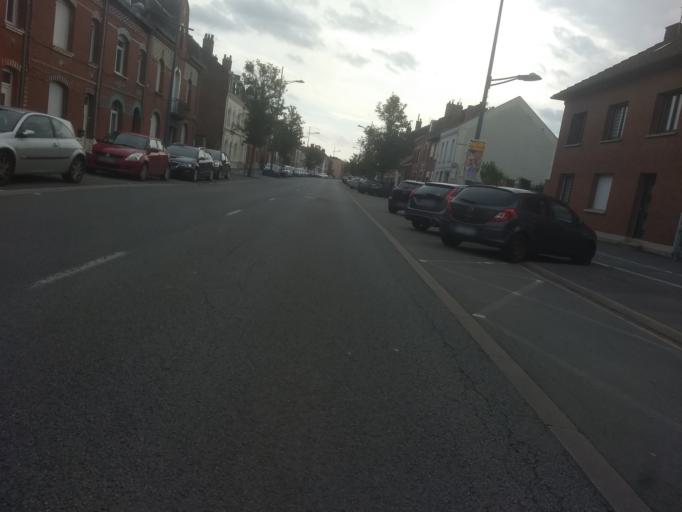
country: FR
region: Nord-Pas-de-Calais
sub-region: Departement du Pas-de-Calais
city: Beaurains
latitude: 50.2747
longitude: 2.7833
